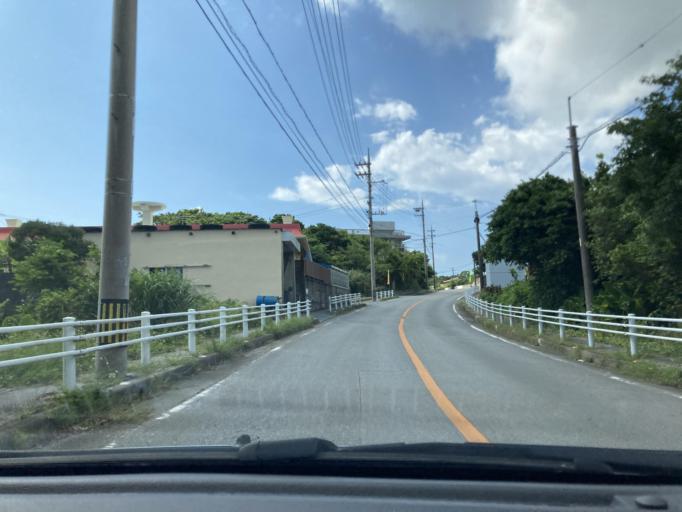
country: JP
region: Okinawa
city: Tomigusuku
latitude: 26.1501
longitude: 127.7915
